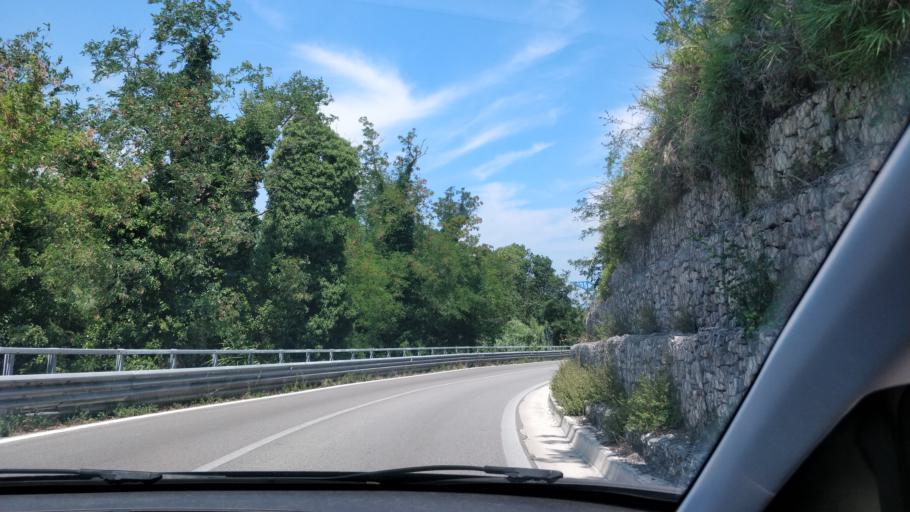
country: IT
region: Abruzzo
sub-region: Provincia di Chieti
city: Ortona
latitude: 42.3408
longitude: 14.4107
